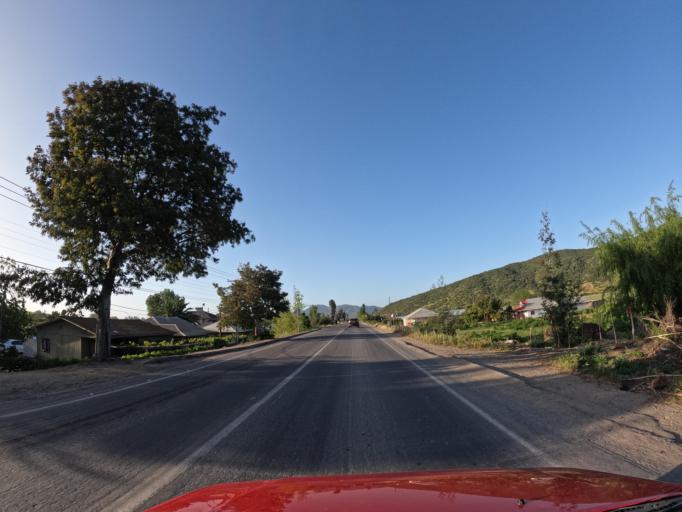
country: CL
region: O'Higgins
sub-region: Provincia de Colchagua
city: Santa Cruz
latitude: -34.4145
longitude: -71.3729
